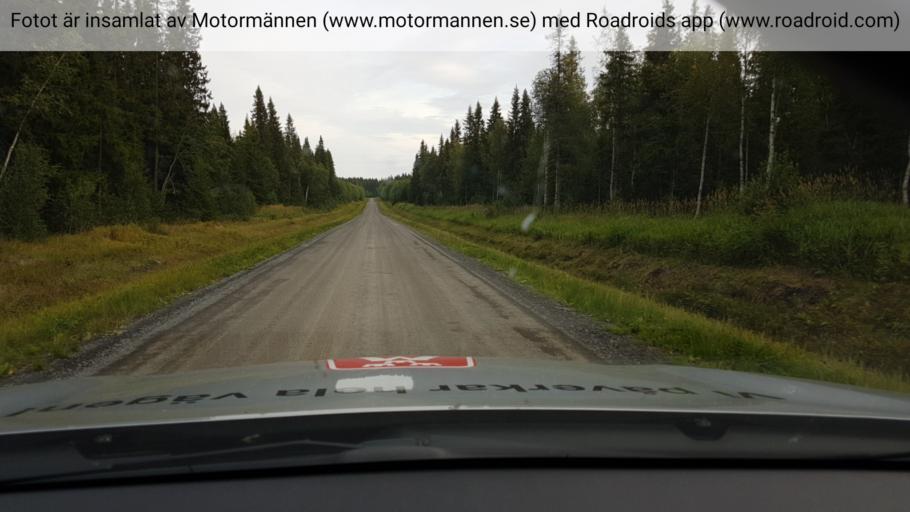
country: SE
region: Jaemtland
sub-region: OEstersunds Kommun
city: Lit
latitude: 63.6515
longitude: 14.9379
